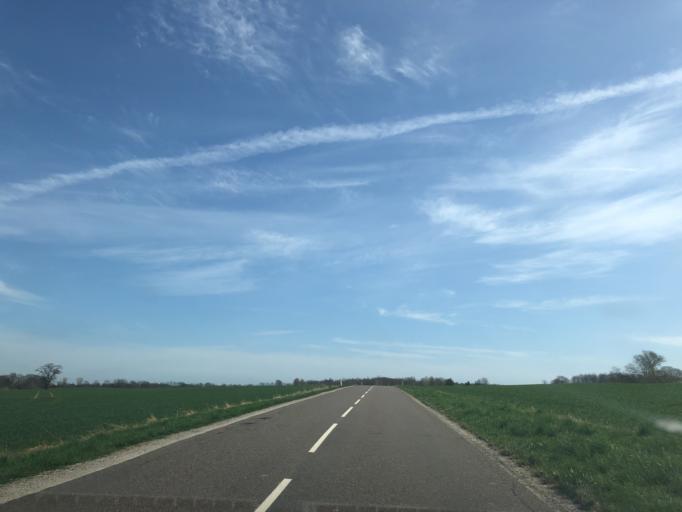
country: DK
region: Zealand
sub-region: Faxe Kommune
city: Fakse
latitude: 55.2891
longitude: 12.0735
